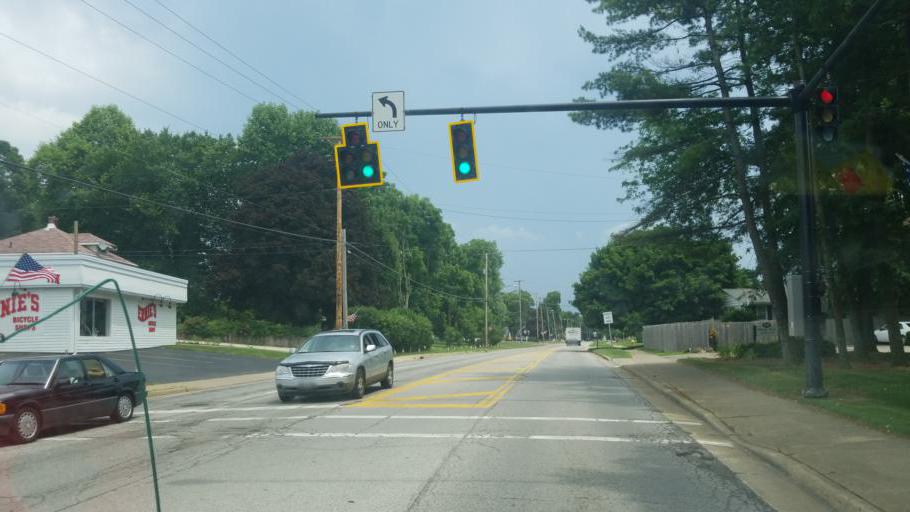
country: US
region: Ohio
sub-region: Stark County
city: North Canton
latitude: 40.8820
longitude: -81.4169
